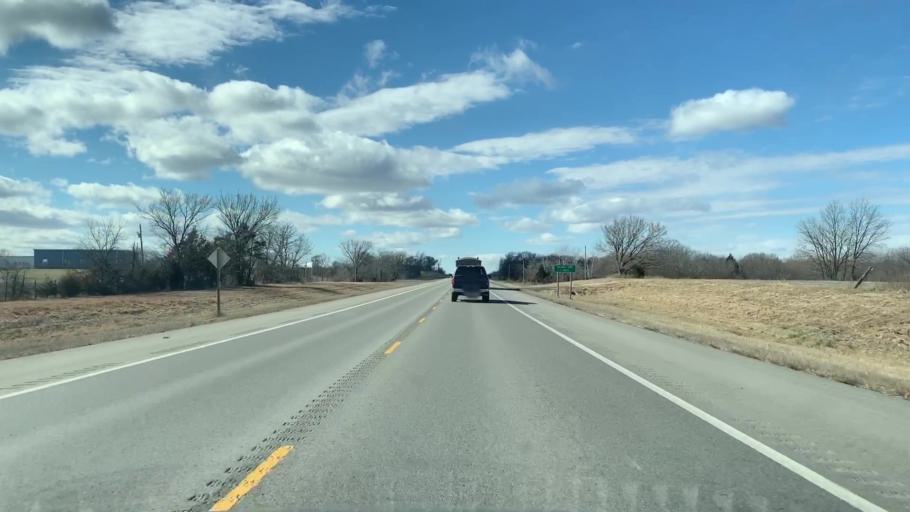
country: US
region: Kansas
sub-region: Cherokee County
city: Columbus
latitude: 37.3399
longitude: -94.8891
